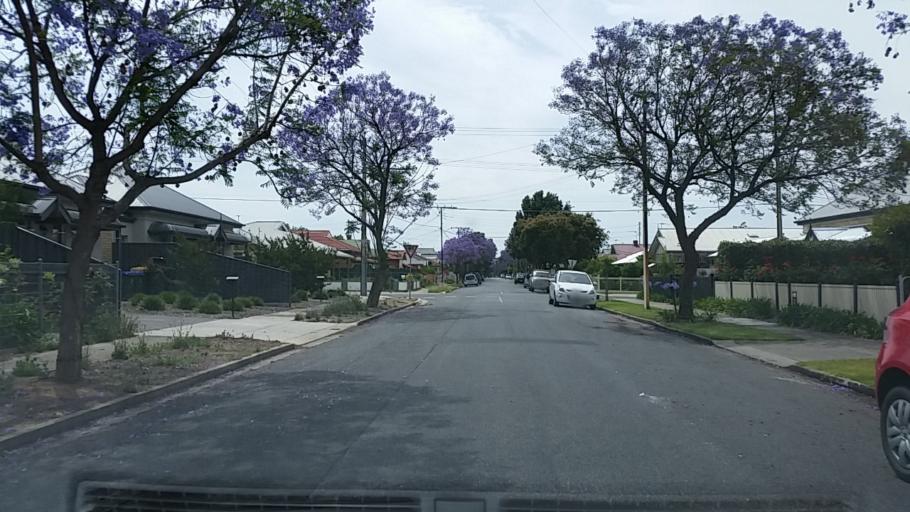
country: AU
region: South Australia
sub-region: Charles Sturt
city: Allenby Gardens
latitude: -34.8919
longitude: 138.5660
